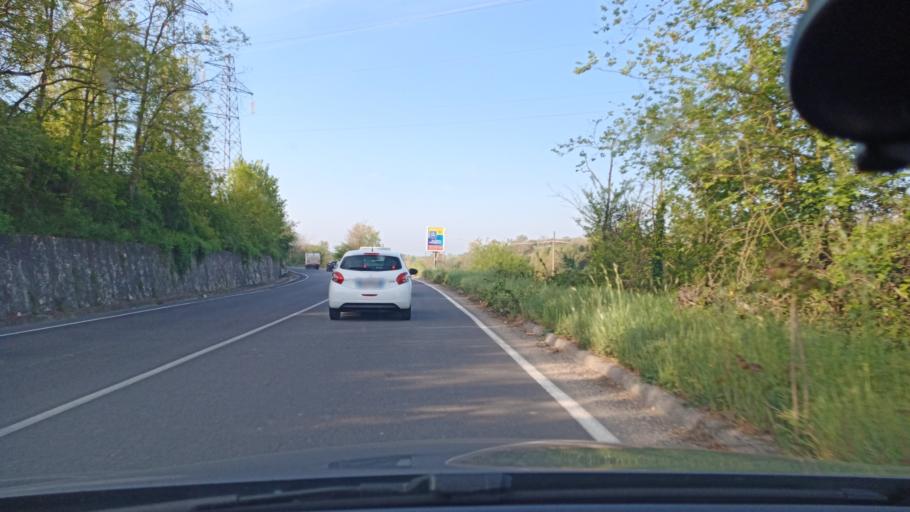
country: IT
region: Latium
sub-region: Citta metropolitana di Roma Capitale
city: Fiano Romano
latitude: 42.1763
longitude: 12.6368
